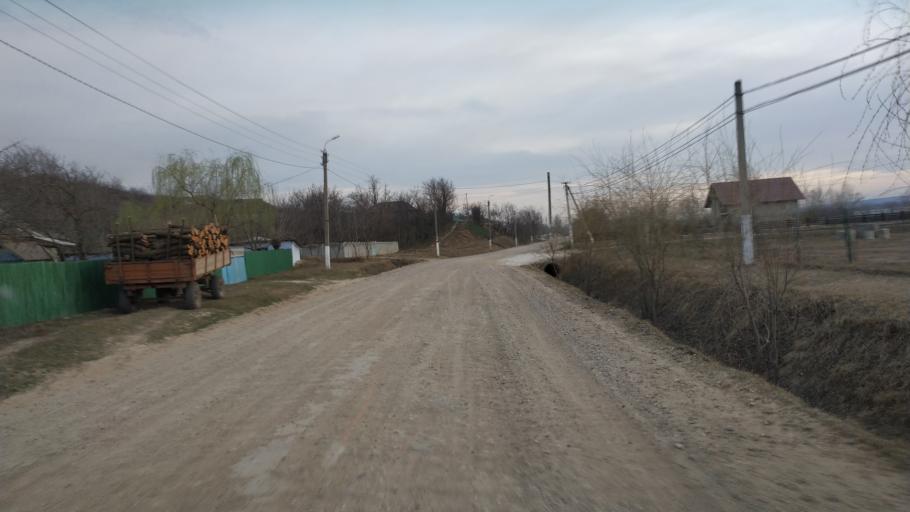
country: MD
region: Hincesti
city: Dancu
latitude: 46.7591
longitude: 28.2089
